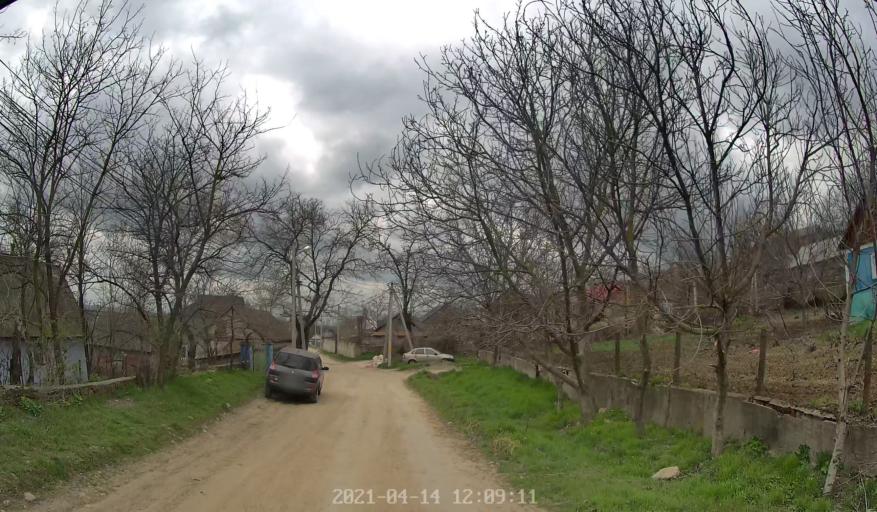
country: MD
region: Criuleni
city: Criuleni
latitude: 47.1708
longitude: 29.2101
